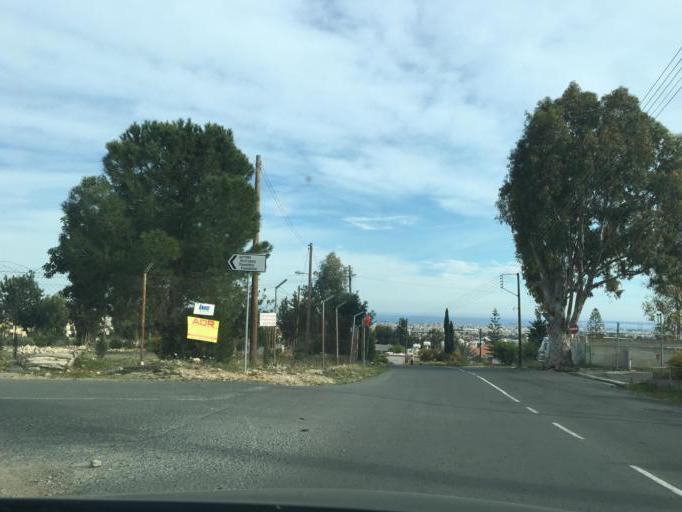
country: CY
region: Limassol
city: Pano Polemidia
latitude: 34.7105
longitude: 33.0050
